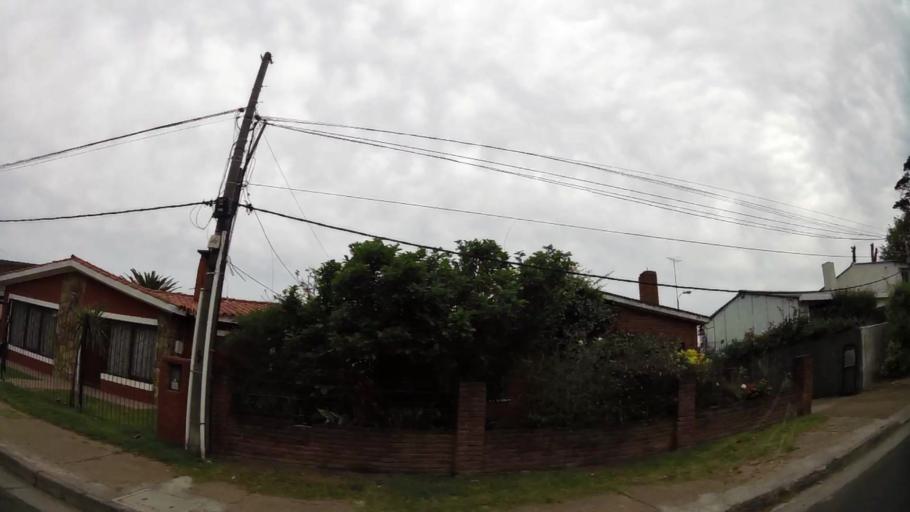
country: UY
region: Maldonado
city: Maldonado
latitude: -34.9121
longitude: -54.9679
